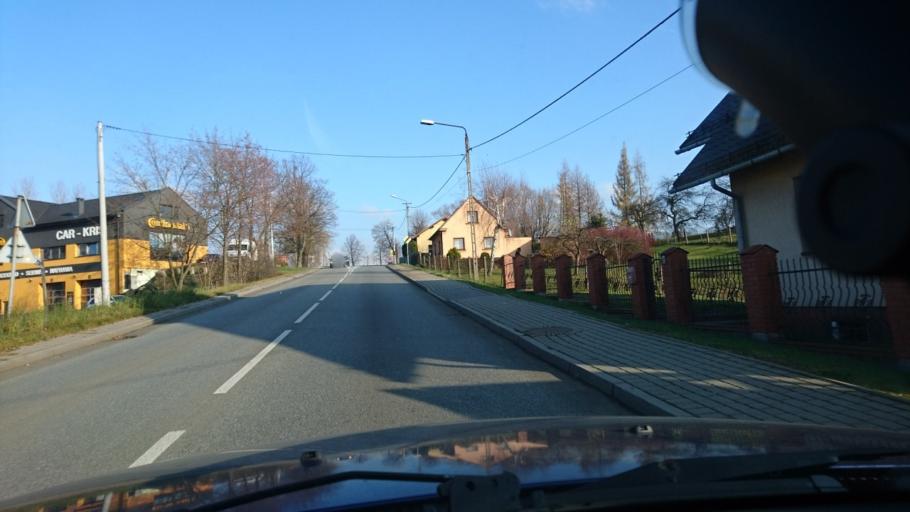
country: PL
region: Silesian Voivodeship
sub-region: Powiat cieszynski
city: Cieszyn
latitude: 49.7515
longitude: 18.6633
